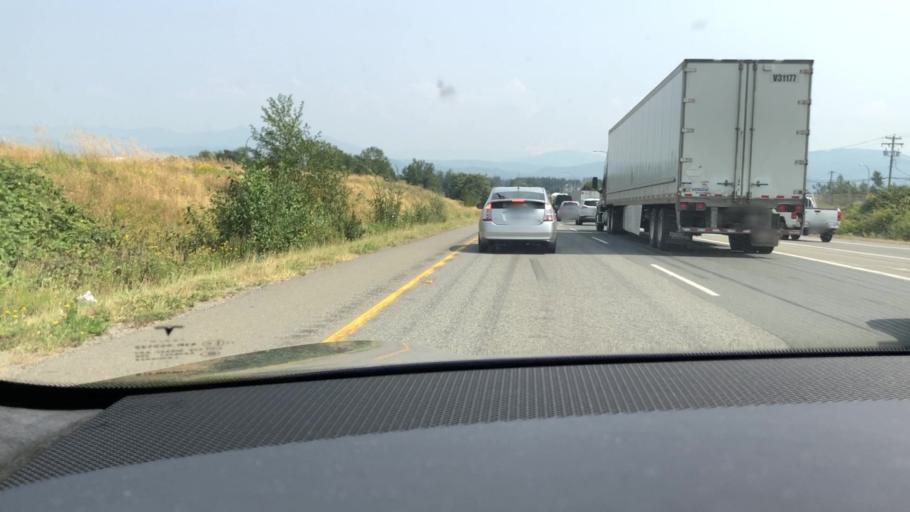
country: CA
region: British Columbia
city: Aldergrove
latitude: 49.0545
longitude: -122.3738
